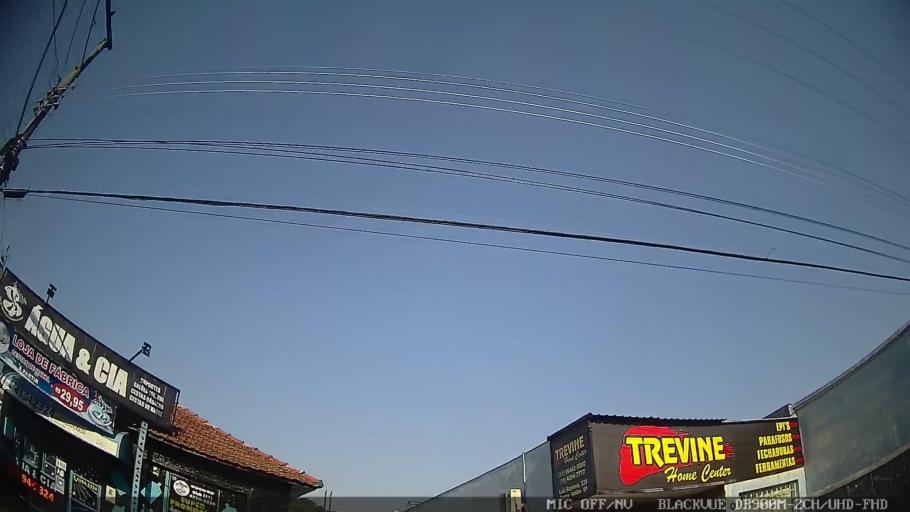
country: BR
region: Sao Paulo
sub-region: Itatiba
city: Itatiba
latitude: -23.0107
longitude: -46.8435
